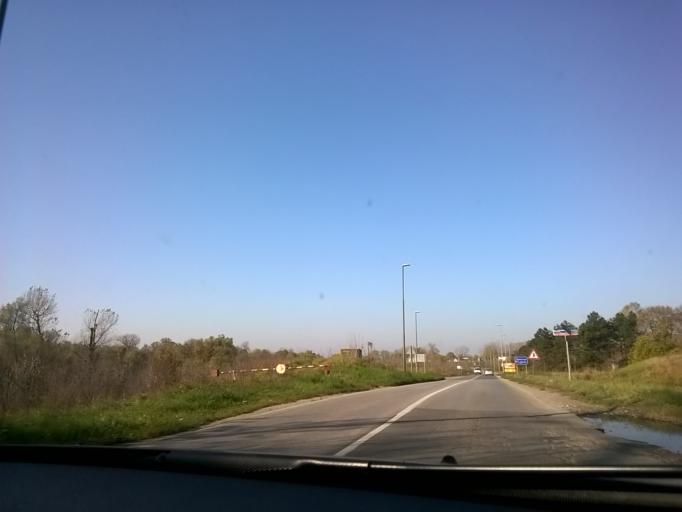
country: RS
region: Autonomna Pokrajina Vojvodina
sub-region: Juznobanatski Okrug
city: Pancevo
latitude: 44.8692
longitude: 20.6216
